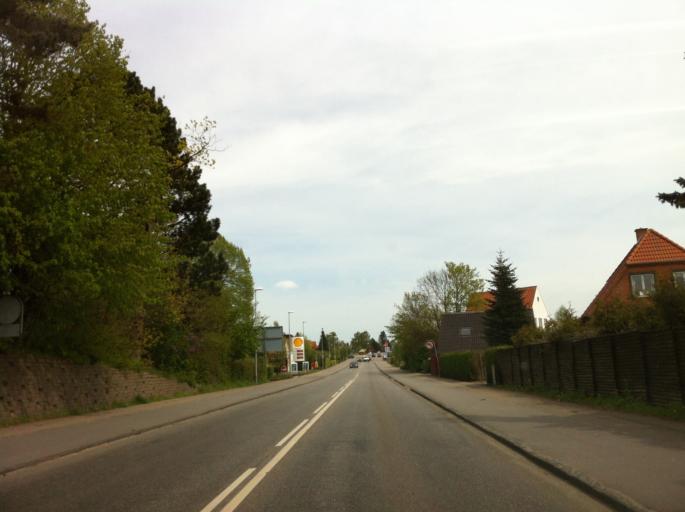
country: DK
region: Zealand
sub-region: Naestved Kommune
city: Naestved
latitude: 55.2473
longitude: 11.7615
